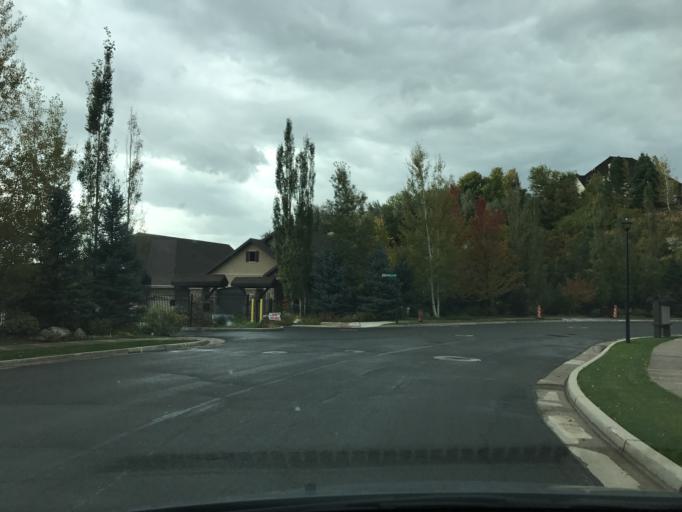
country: US
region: Utah
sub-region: Davis County
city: Fruit Heights
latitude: 41.0177
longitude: -111.9003
